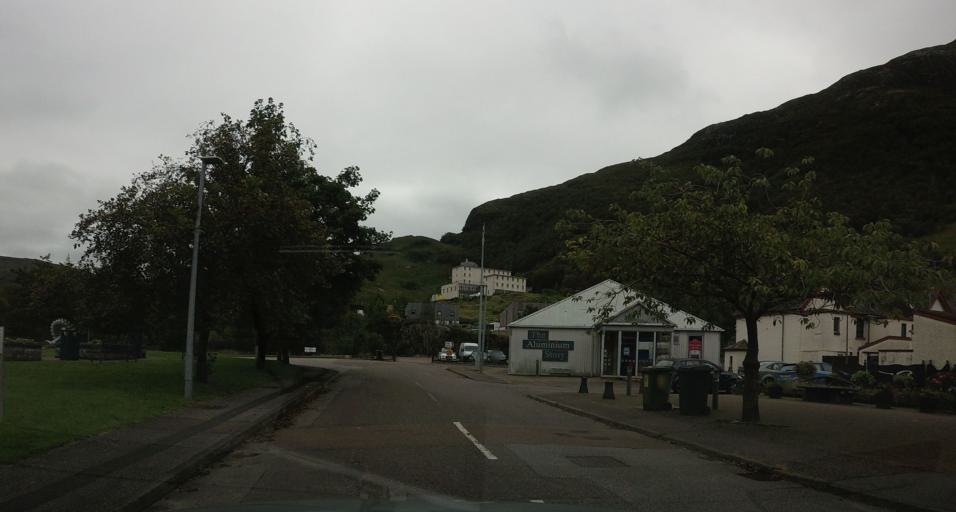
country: GB
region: Scotland
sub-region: Highland
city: Fort William
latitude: 56.7133
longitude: -4.9629
